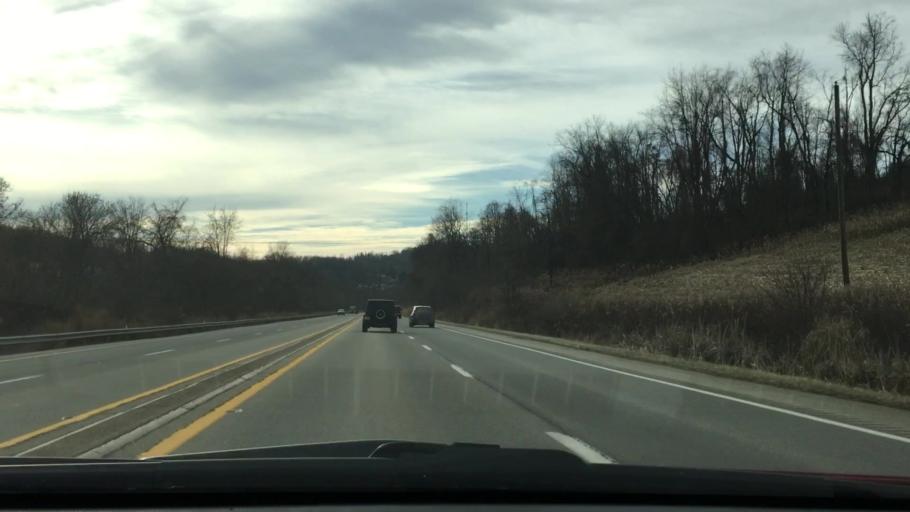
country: US
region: Pennsylvania
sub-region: Fayette County
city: Perryopolis
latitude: 40.0362
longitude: -79.7700
